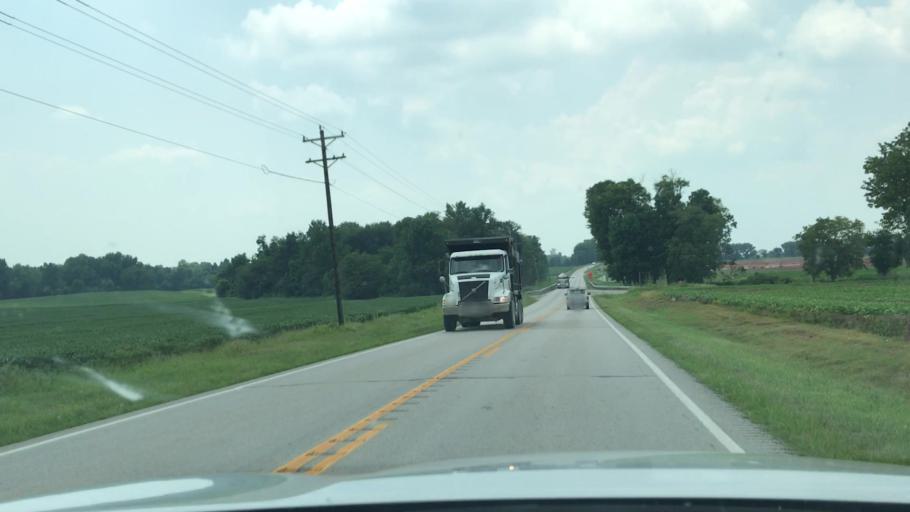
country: US
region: Kentucky
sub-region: Todd County
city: Guthrie
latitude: 36.6629
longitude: -87.1690
